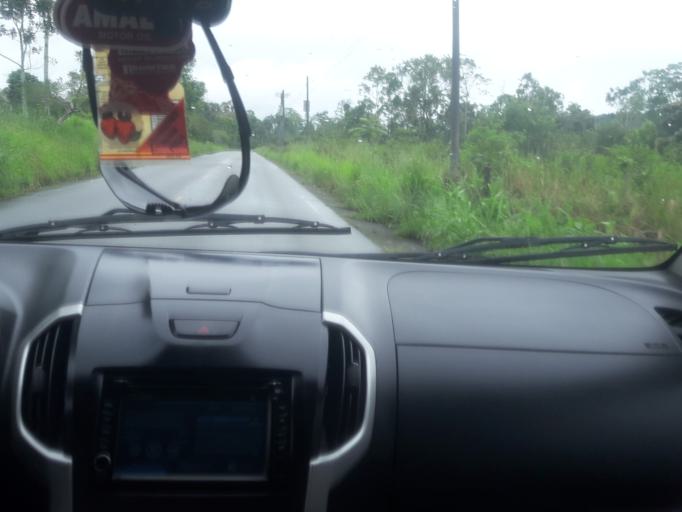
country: EC
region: Napo
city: Tena
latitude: -1.0336
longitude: -77.6772
